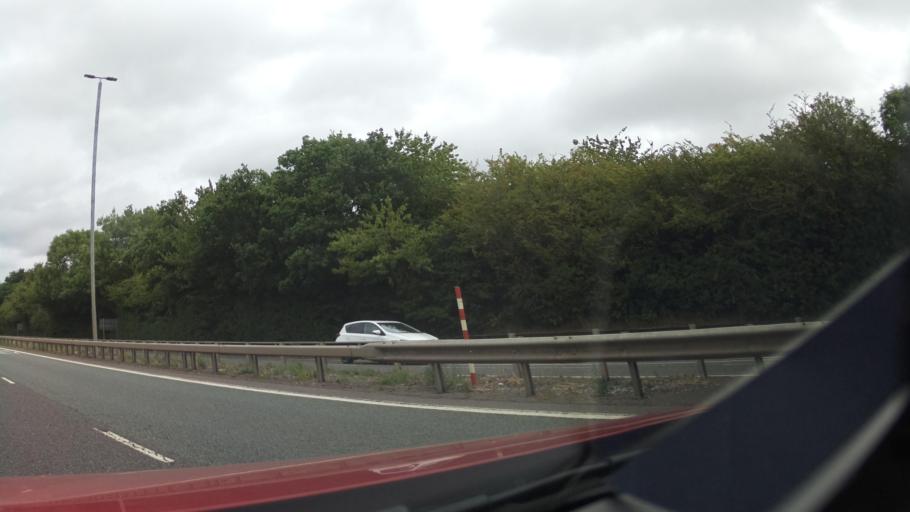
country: GB
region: England
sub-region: Nottinghamshire
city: Eastwood
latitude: 53.0134
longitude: -1.3161
